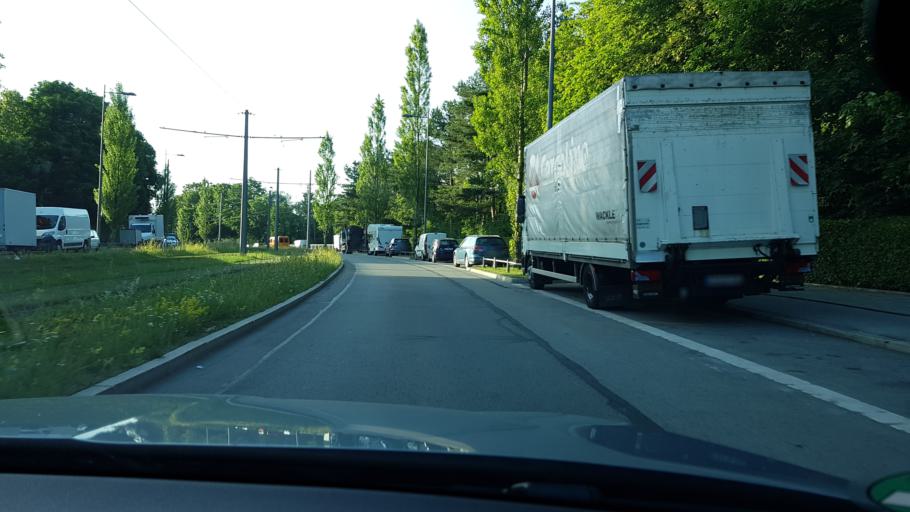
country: DE
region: Bavaria
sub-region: Upper Bavaria
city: Unterfoehring
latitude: 48.1734
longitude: 11.6368
